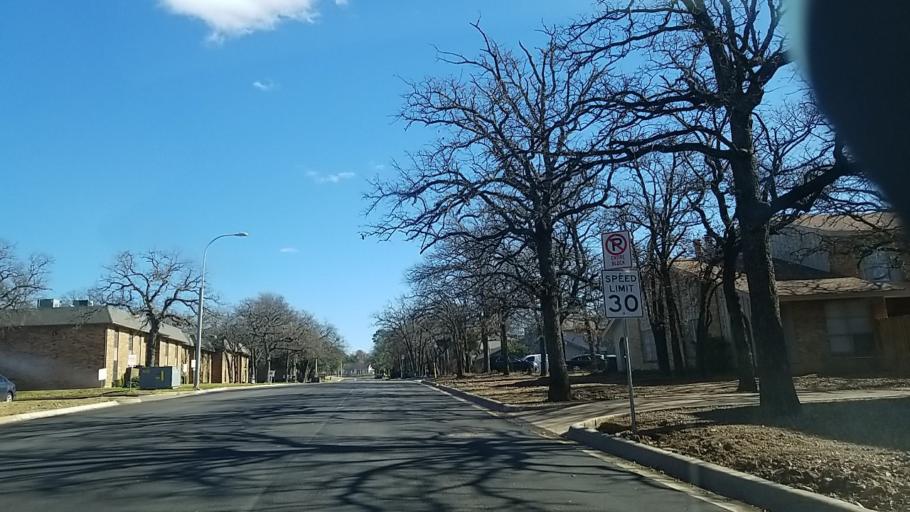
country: US
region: Texas
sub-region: Denton County
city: Denton
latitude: 33.1899
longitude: -97.1235
